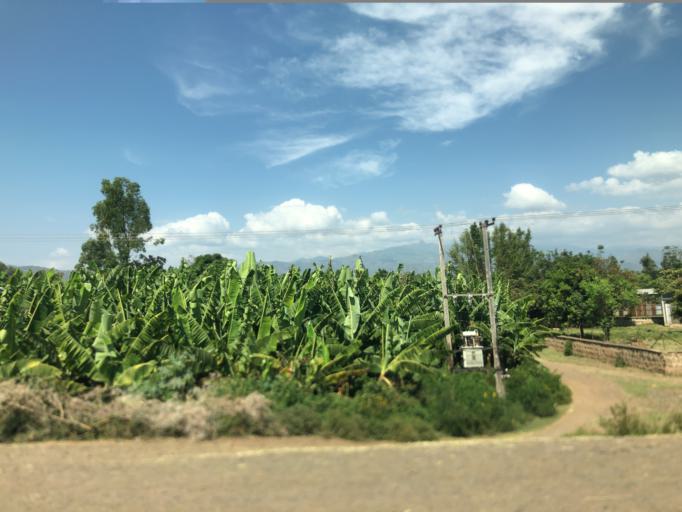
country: ET
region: Southern Nations, Nationalities, and People's Region
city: Arba Minch'
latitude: 5.8513
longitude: 37.4688
